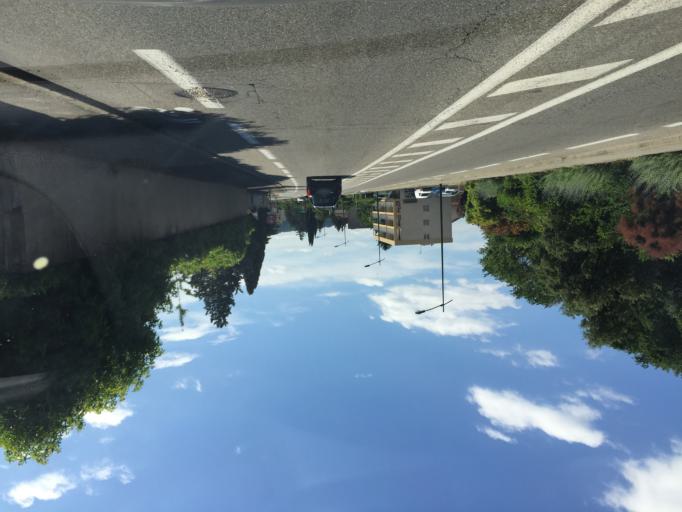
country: FR
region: Rhone-Alpes
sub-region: Departement de l'Ardeche
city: Tournon-sur-Rhone
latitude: 45.0602
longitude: 4.8418
